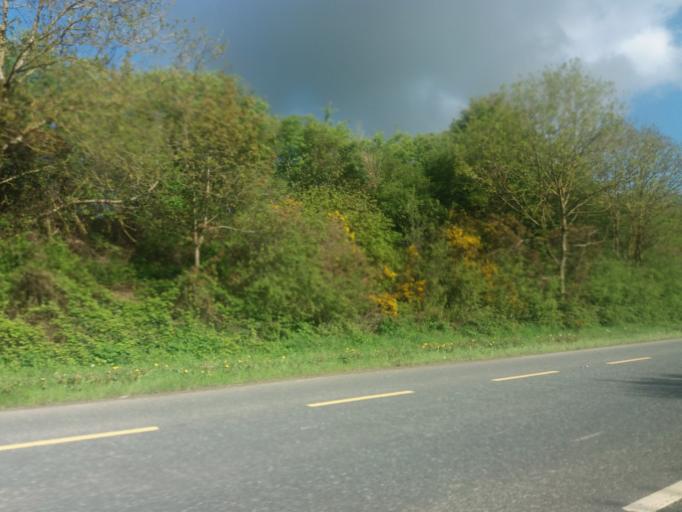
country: IE
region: Leinster
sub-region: Loch Garman
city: Enniscorthy
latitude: 52.5294
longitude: -6.5573
